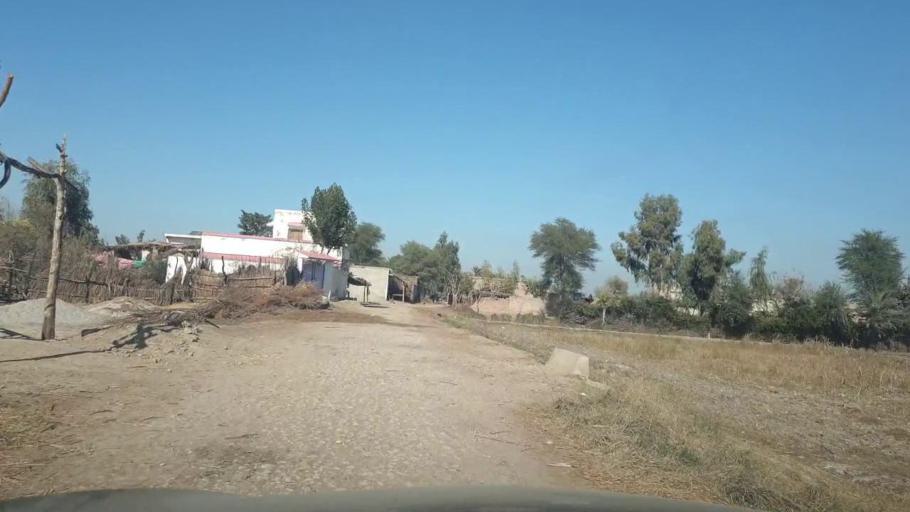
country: PK
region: Sindh
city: Mirpur Mathelo
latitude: 28.0809
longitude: 69.4893
